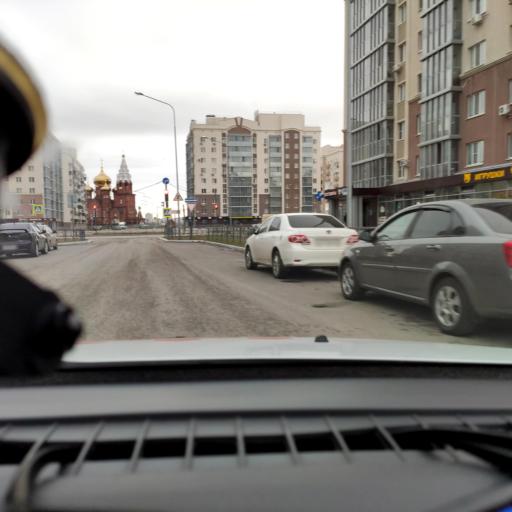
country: RU
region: Samara
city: Samara
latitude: 53.1138
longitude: 50.1455
